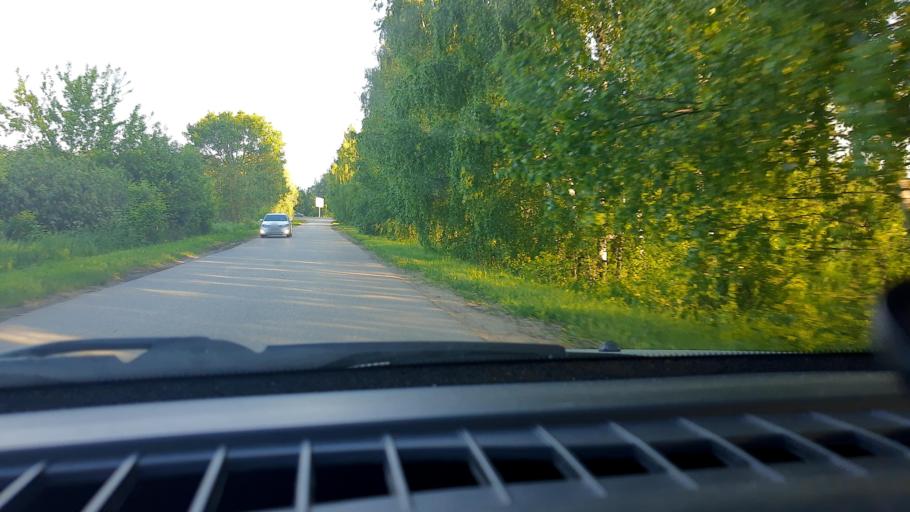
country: RU
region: Nizjnij Novgorod
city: Afonino
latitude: 56.2238
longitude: 44.0595
